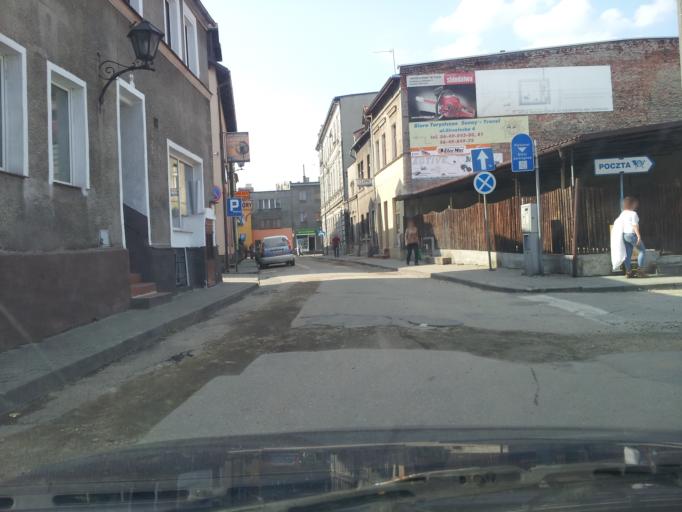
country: PL
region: Kujawsko-Pomorskie
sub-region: Powiat brodnicki
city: Brodnica
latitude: 53.2549
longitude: 19.4045
